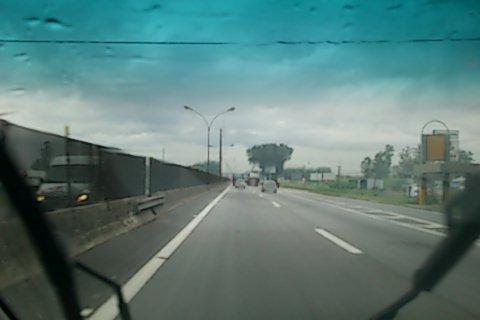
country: BR
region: Sao Paulo
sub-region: Jacarei
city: Jacarei
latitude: -23.2664
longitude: -45.9607
